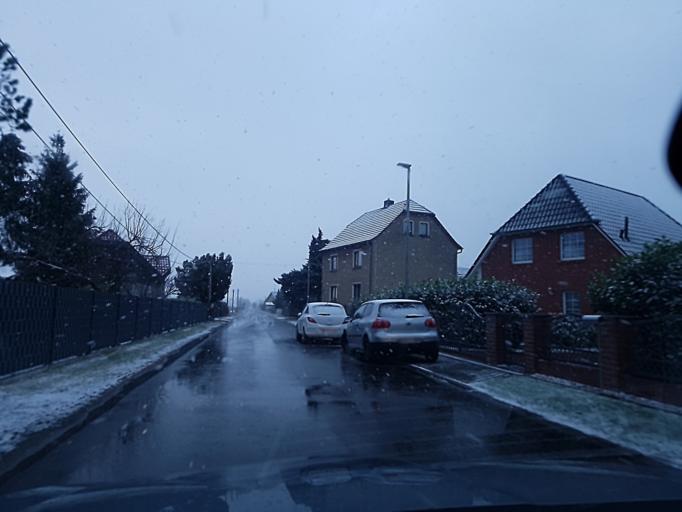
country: DE
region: Brandenburg
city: Elsterwerda
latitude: 51.4478
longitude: 13.5296
